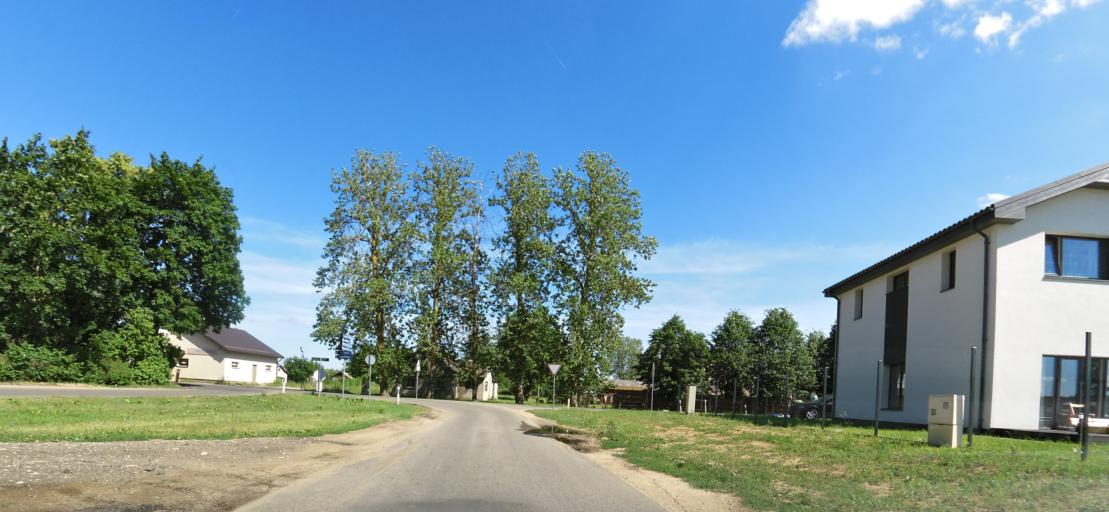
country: LT
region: Vilnius County
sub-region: Vilnius
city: Fabijoniskes
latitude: 54.8013
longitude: 25.3460
